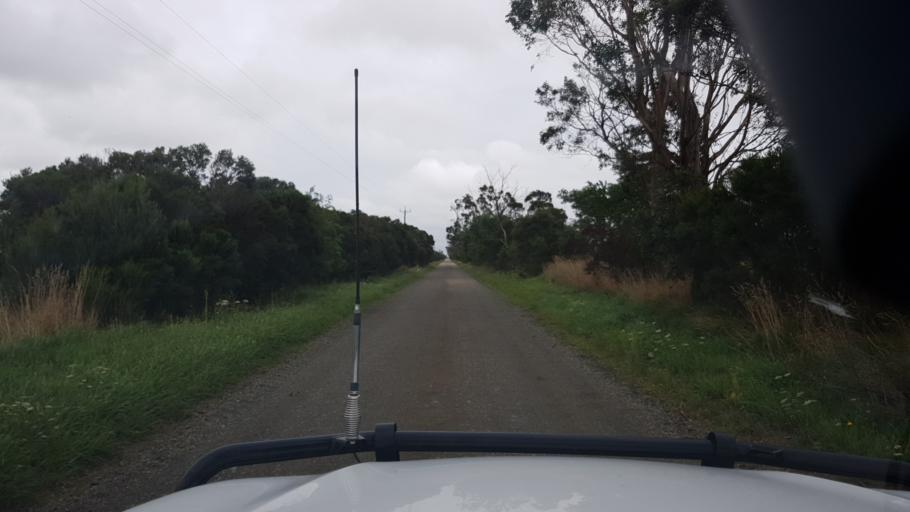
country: AU
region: Victoria
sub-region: Cardinia
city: Bunyip
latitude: -38.1603
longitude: 145.7159
